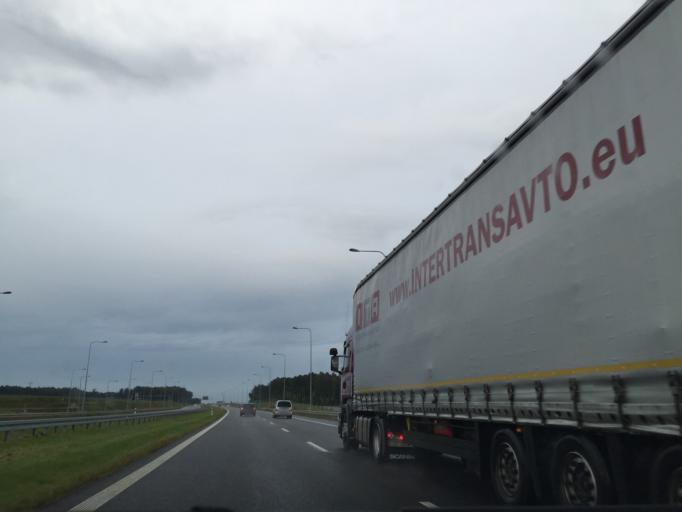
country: PL
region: Podlasie
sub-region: Powiat zambrowski
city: Rutki-Kossaki
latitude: 53.0384
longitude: 22.3552
